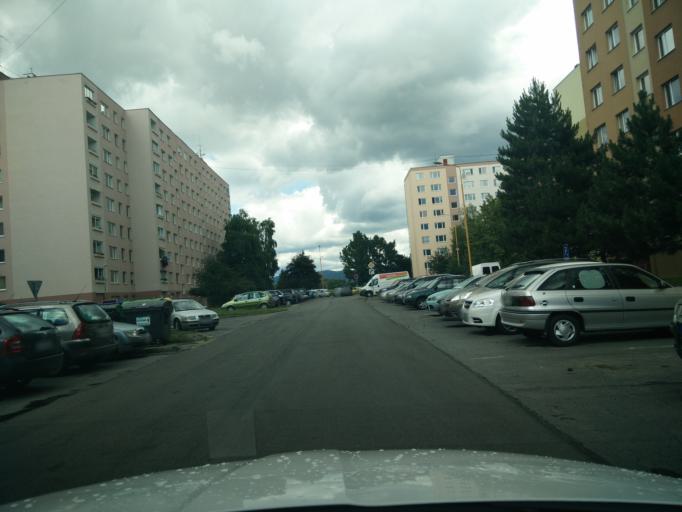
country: SK
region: Nitriansky
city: Prievidza
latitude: 48.7851
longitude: 18.6179
